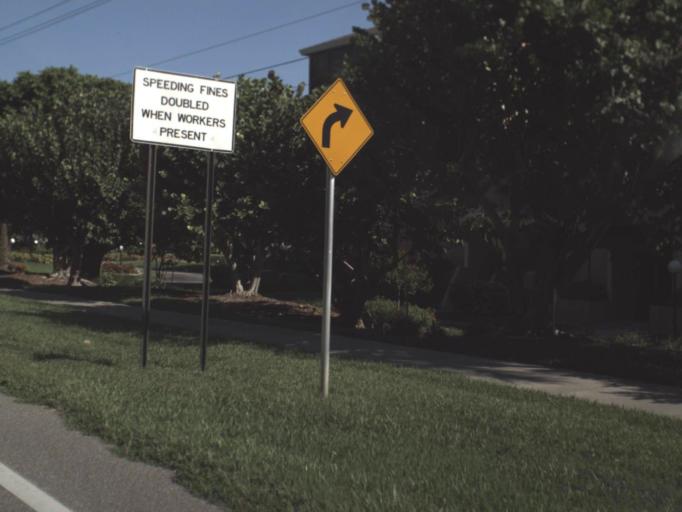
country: US
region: Florida
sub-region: Manatee County
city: Longboat Key
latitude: 27.3788
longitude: -82.6350
